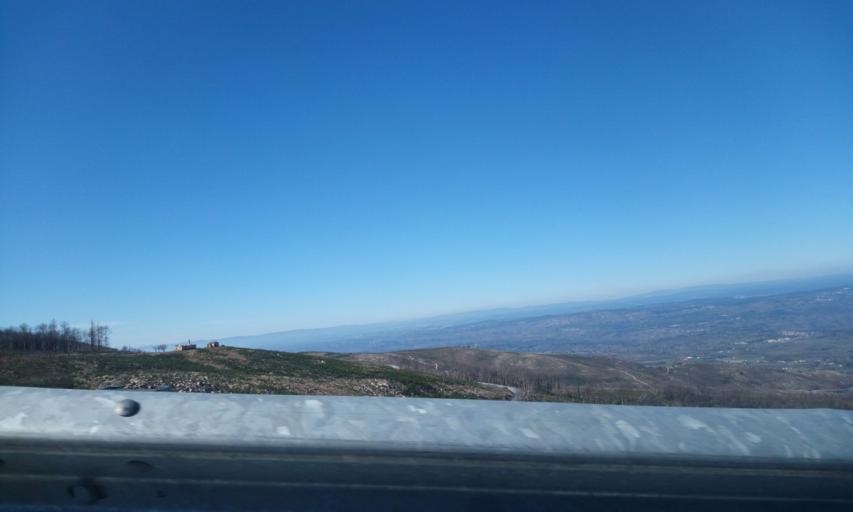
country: PT
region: Guarda
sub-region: Manteigas
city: Manteigas
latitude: 40.4933
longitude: -7.5241
